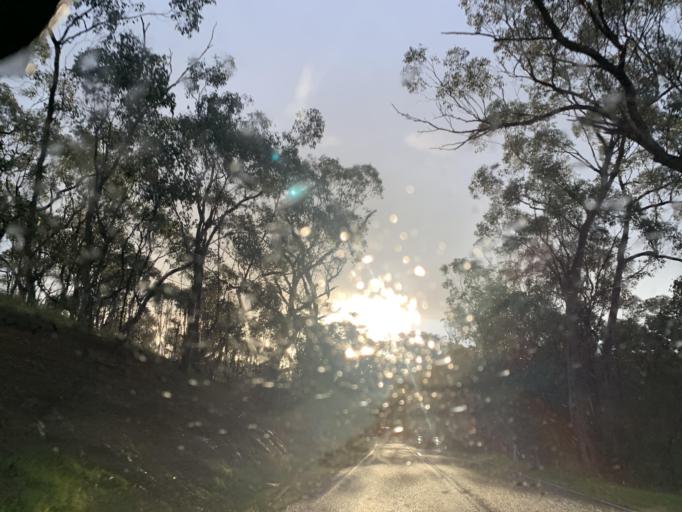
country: AU
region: Victoria
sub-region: Murrindindi
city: Kinglake West
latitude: -37.2102
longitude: 145.0895
